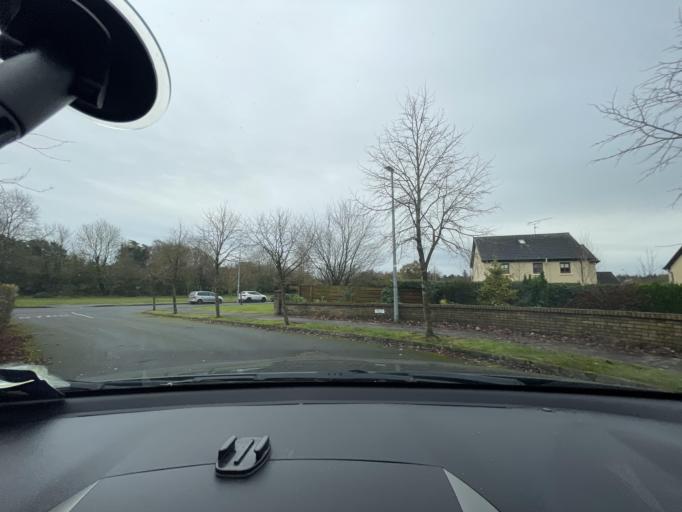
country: IE
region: Ulster
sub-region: An Cabhan
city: Virginia
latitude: 53.8398
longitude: -7.1005
